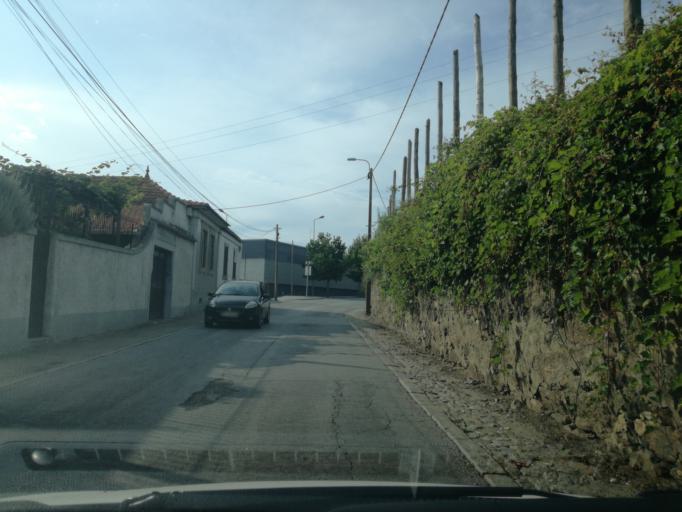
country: PT
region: Porto
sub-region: Vila Nova de Gaia
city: Azenha
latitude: 41.0612
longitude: -8.6277
